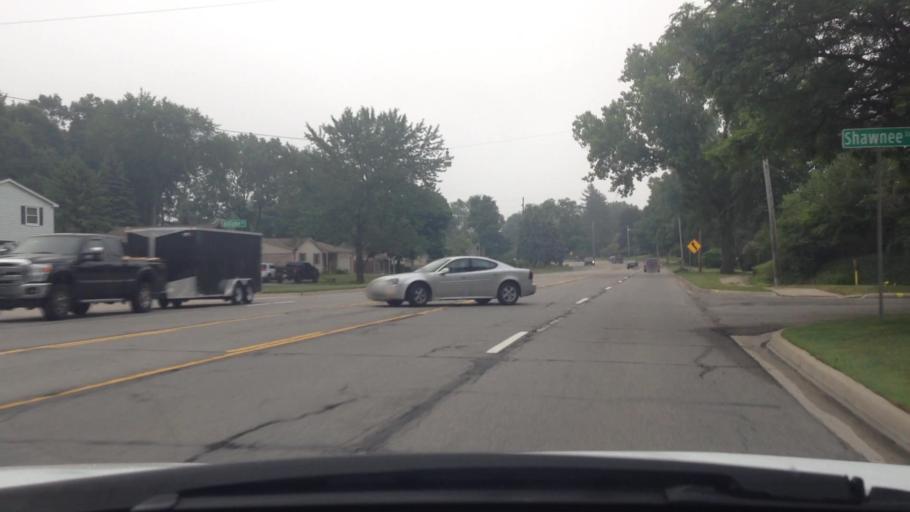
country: US
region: Michigan
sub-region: Oakland County
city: Waterford
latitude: 42.6861
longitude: -83.3448
